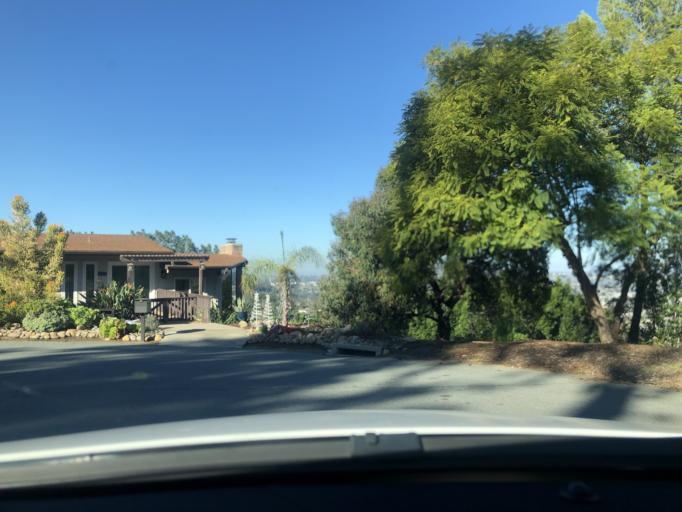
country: US
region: California
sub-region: San Diego County
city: Casa de Oro-Mount Helix
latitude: 32.7709
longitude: -116.9516
